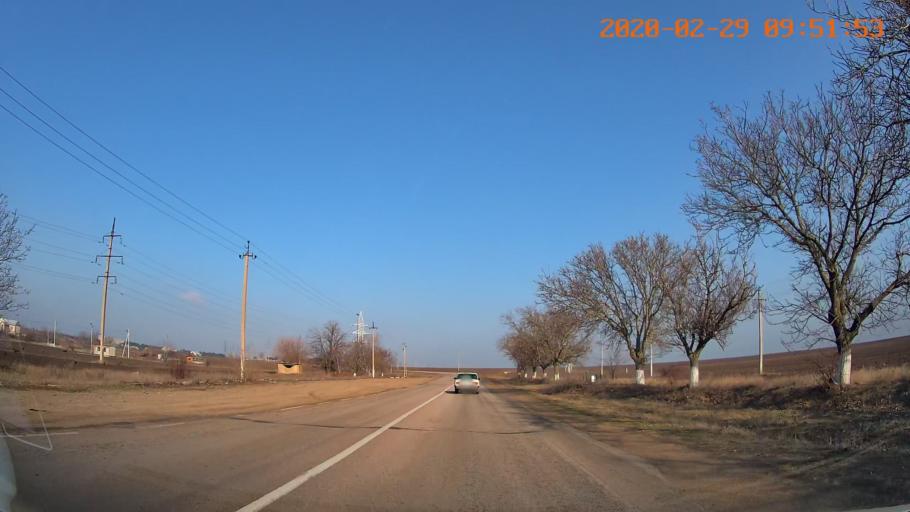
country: MD
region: Telenesti
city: Slobozia
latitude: 46.7123
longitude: 29.7351
